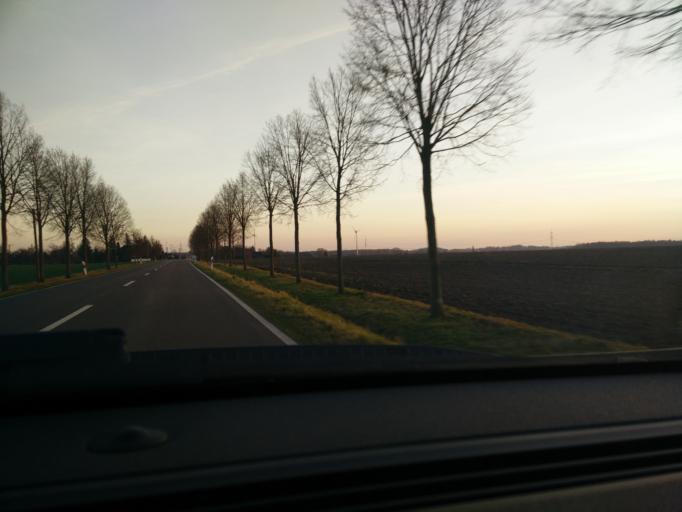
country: DE
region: Saxony
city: Geithain
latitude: 51.1073
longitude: 12.6913
